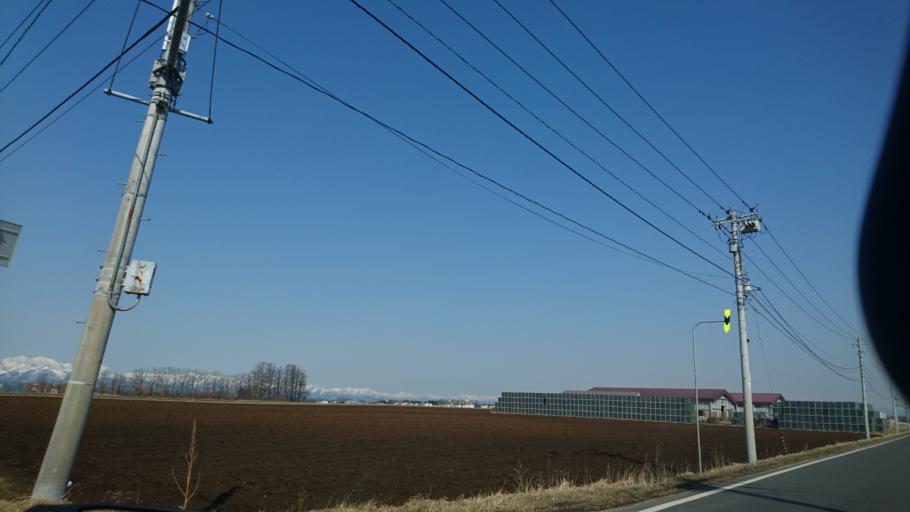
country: JP
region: Hokkaido
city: Obihiro
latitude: 42.9034
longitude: 143.0849
